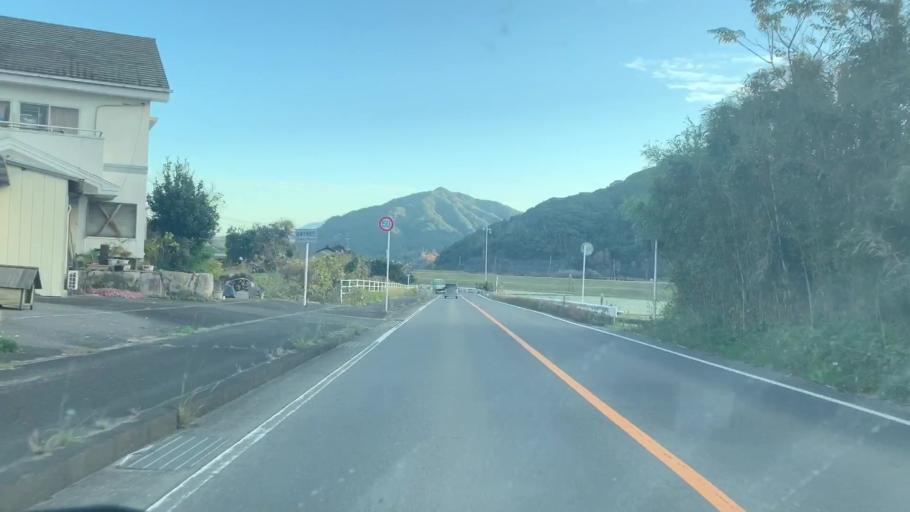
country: JP
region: Saga Prefecture
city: Karatsu
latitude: 33.3830
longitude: 129.9892
